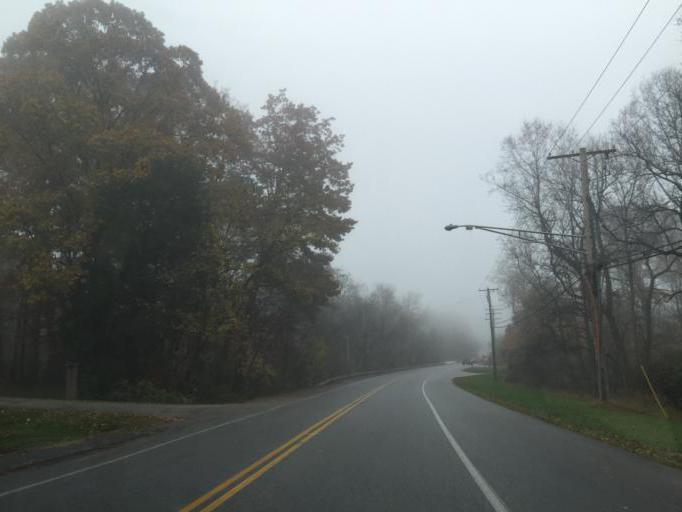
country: US
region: Maryland
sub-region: Howard County
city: Columbia
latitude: 39.2460
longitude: -76.8482
